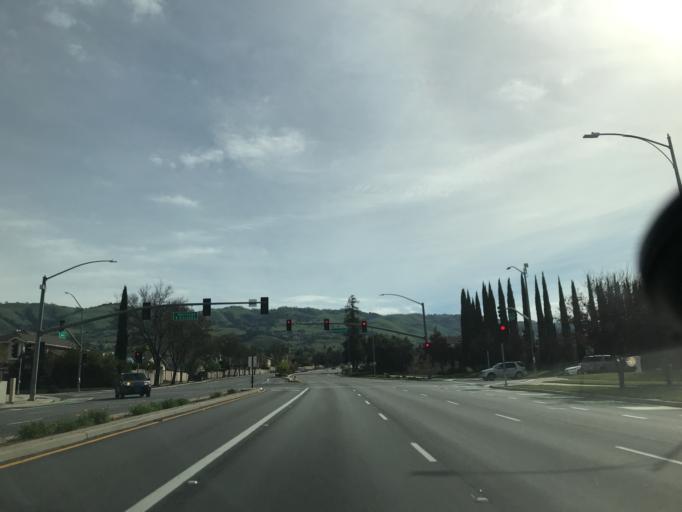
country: US
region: California
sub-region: Santa Clara County
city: Seven Trees
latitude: 37.3157
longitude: -121.7802
